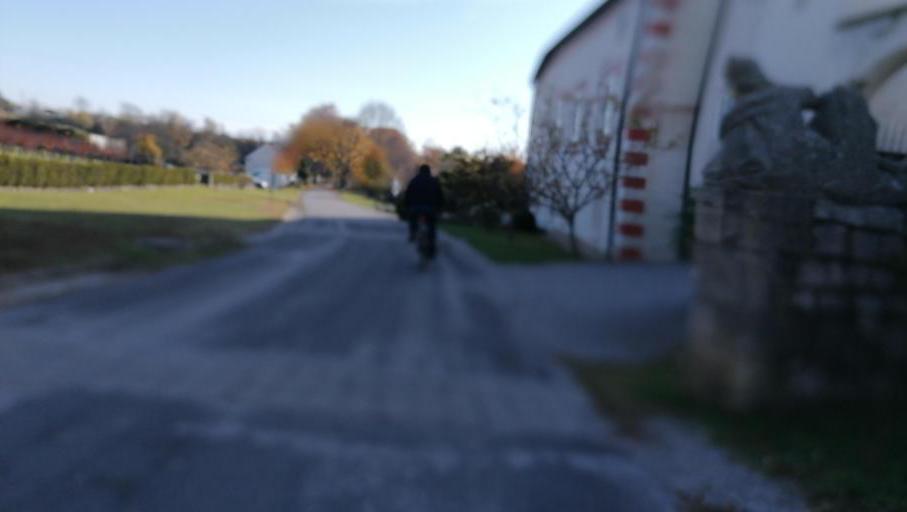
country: AT
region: Lower Austria
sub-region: Politischer Bezirk Modling
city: Gumpoldskirchen
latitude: 48.0523
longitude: 16.2927
